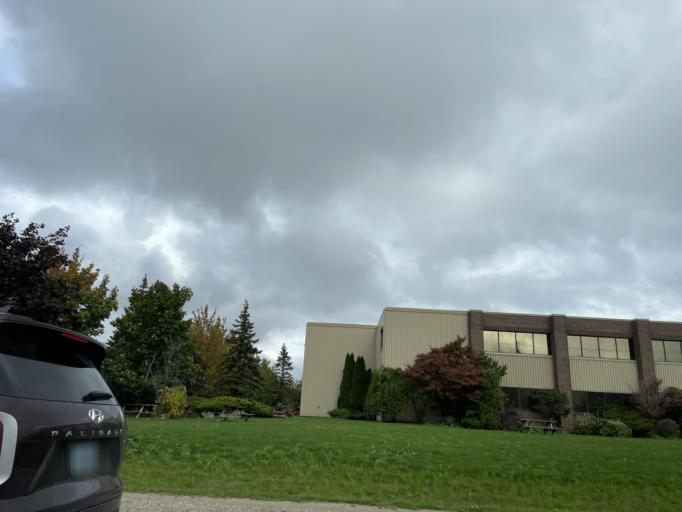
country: CA
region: Ontario
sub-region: Wellington County
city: Guelph
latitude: 43.5348
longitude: -80.3093
